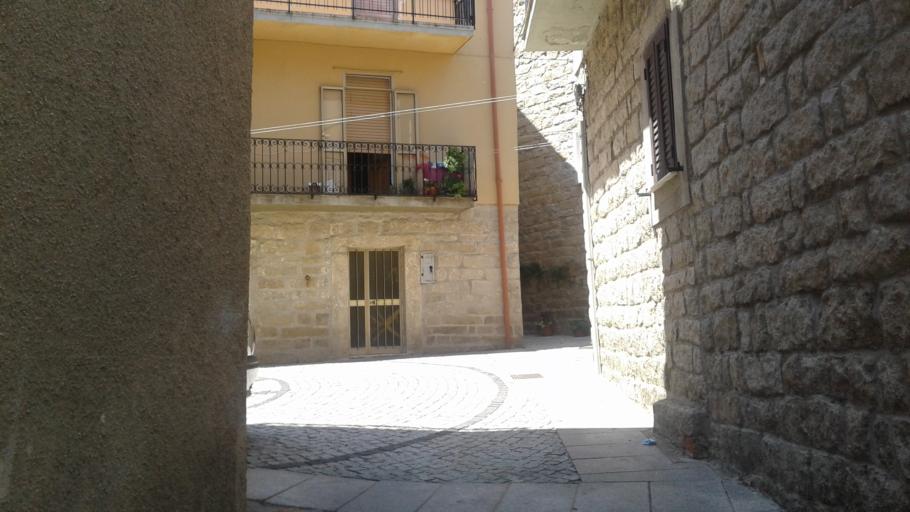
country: IT
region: Sardinia
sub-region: Provincia di Olbia-Tempio
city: Aggius
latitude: 40.9292
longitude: 9.0652
